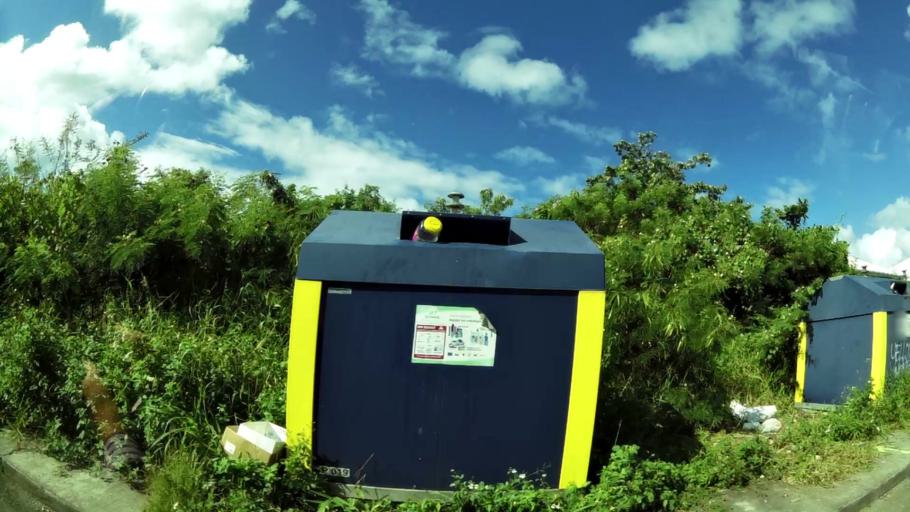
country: GP
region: Guadeloupe
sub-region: Guadeloupe
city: Port-Louis
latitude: 16.4142
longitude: -61.5294
